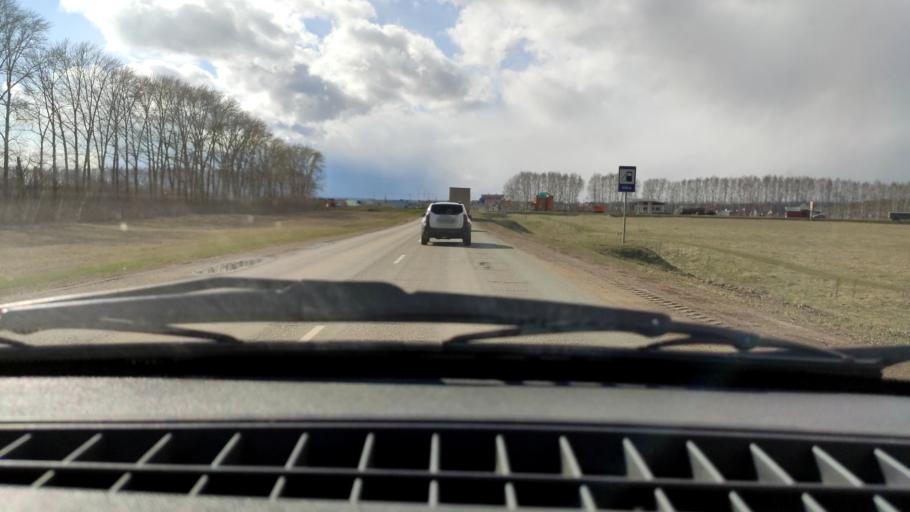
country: RU
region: Bashkortostan
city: Chekmagush
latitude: 55.1291
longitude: 54.6894
